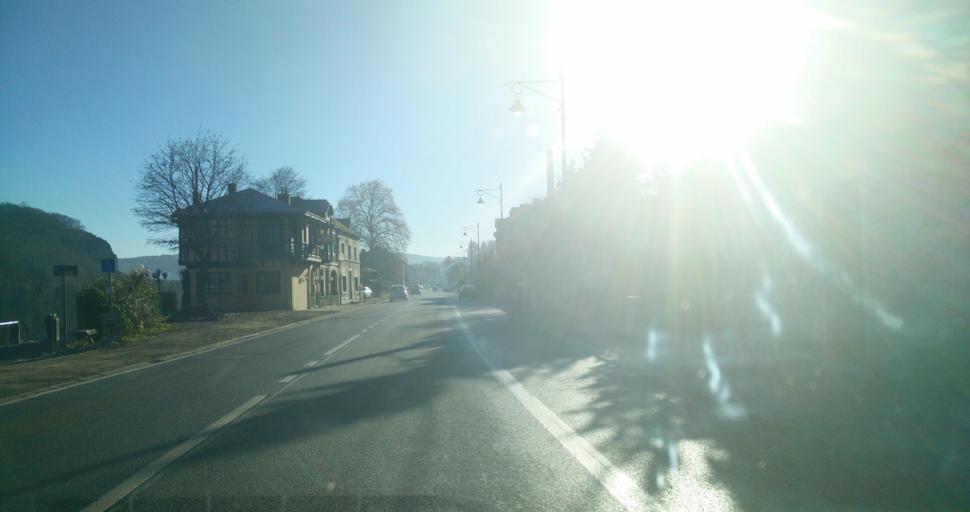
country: BE
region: Wallonia
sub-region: Province de Namur
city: Namur
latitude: 50.4321
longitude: 4.8639
